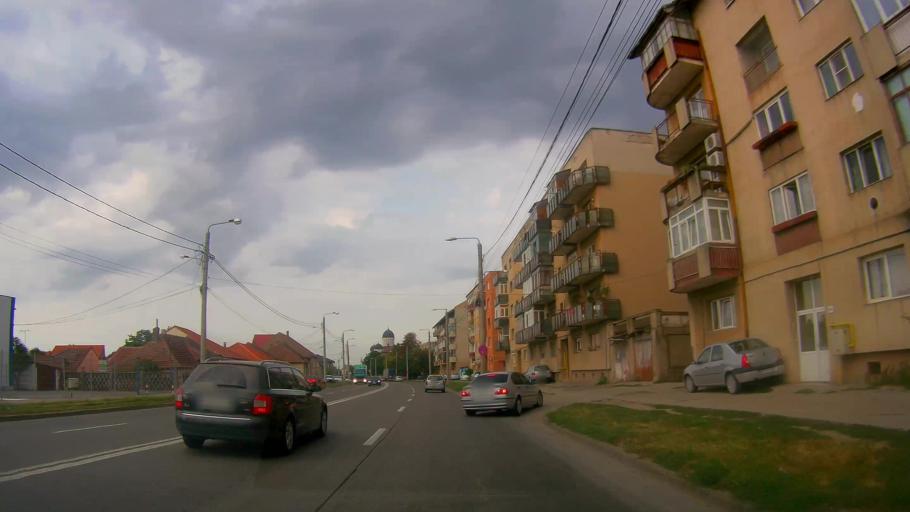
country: RO
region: Satu Mare
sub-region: Municipiul Satu Mare
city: Satu Mare
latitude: 47.7958
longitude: 22.8956
